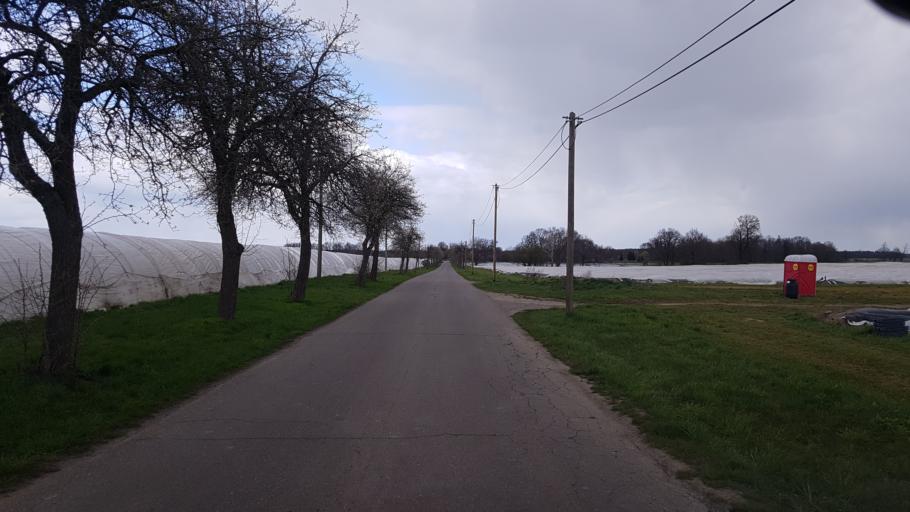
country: DE
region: Brandenburg
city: Calau
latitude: 51.7467
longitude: 14.0028
